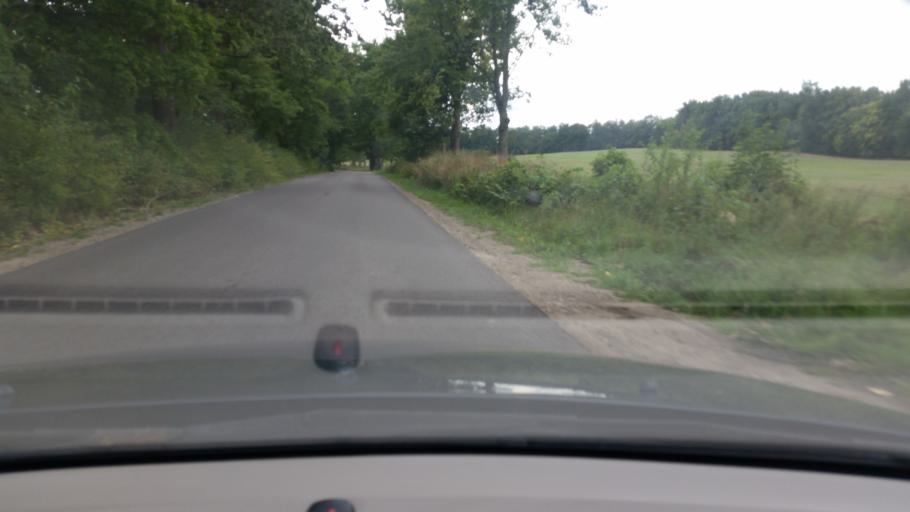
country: PL
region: Pomeranian Voivodeship
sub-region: Powiat wejherowski
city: Choczewo
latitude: 54.7538
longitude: 17.7922
